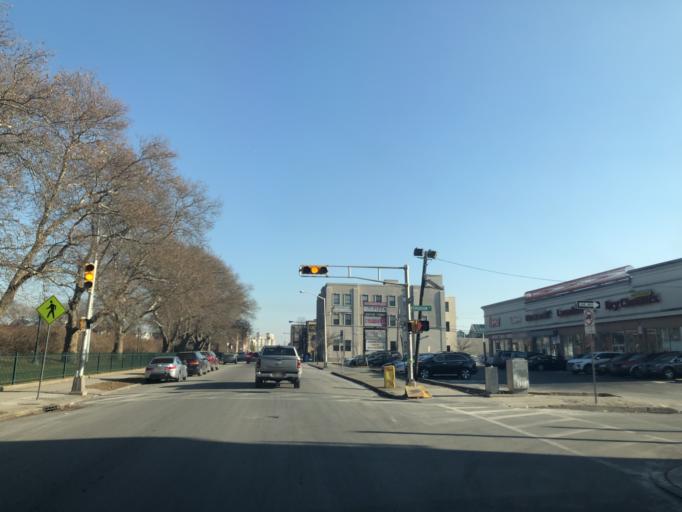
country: US
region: New Jersey
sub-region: Hudson County
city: Harrison
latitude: 40.7314
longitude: -74.1530
